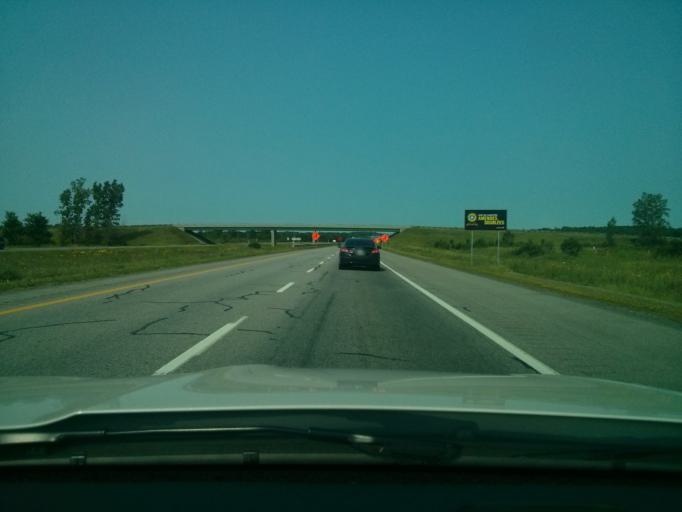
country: CA
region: Quebec
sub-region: Outaouais
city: Gatineau
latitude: 45.5116
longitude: -75.5866
